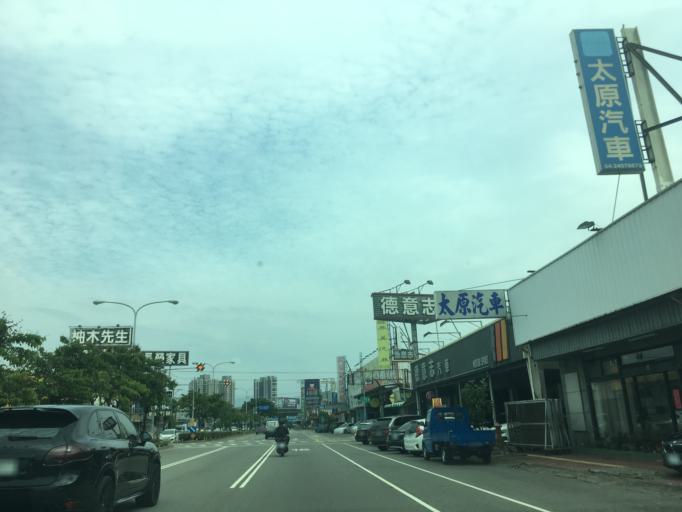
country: TW
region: Taiwan
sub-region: Taichung City
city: Taichung
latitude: 24.1038
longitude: 120.6691
